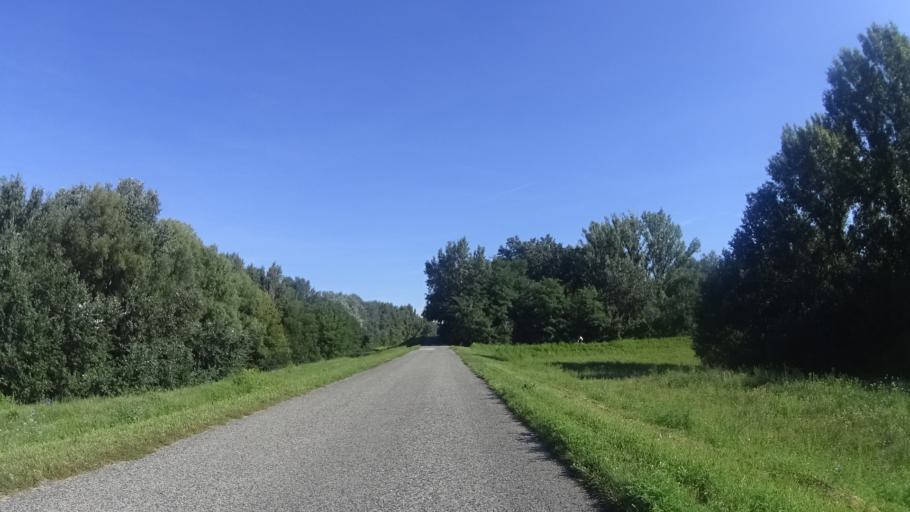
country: SK
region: Bratislavsky
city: Bratislava
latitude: 48.1102
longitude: 17.1463
